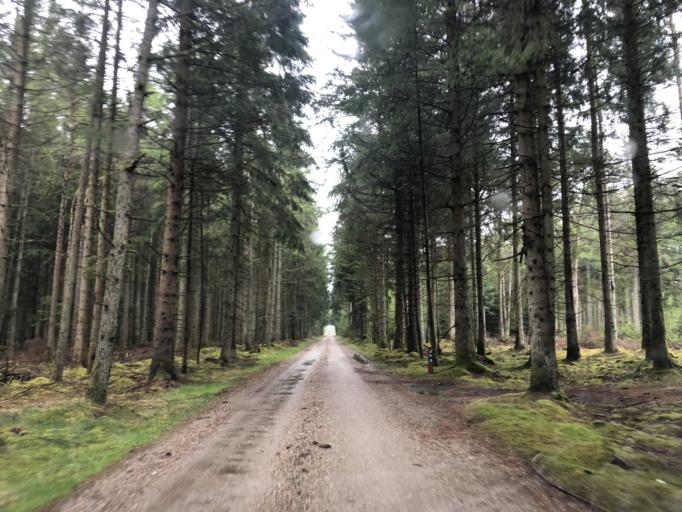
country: DK
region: Central Jutland
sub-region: Lemvig Kommune
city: Lemvig
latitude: 56.4573
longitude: 8.3964
